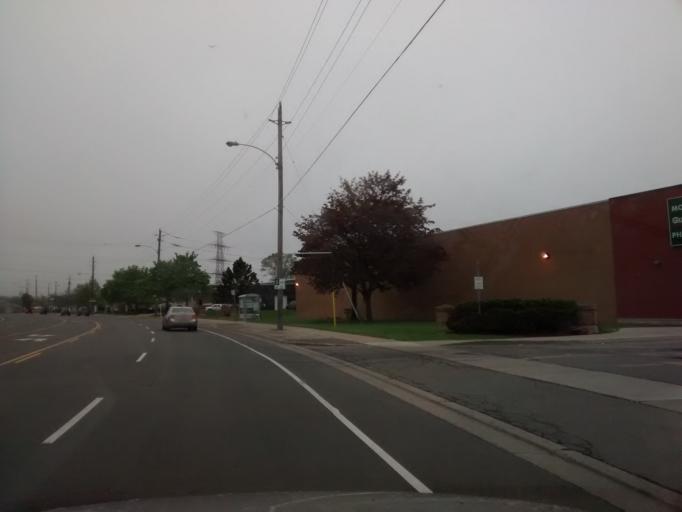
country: CA
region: Ontario
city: Burlington
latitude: 43.3298
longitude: -79.8206
